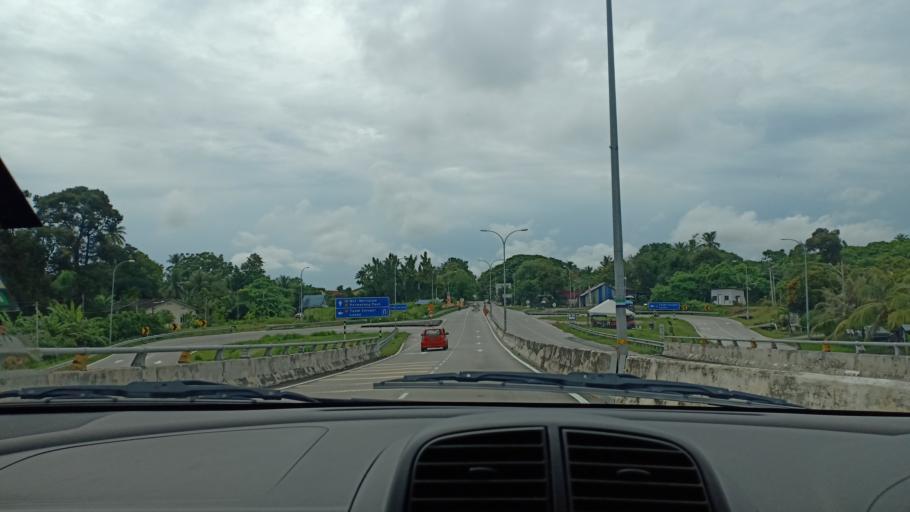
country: MY
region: Penang
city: Bukit Mertajam
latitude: 5.4060
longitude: 100.4717
